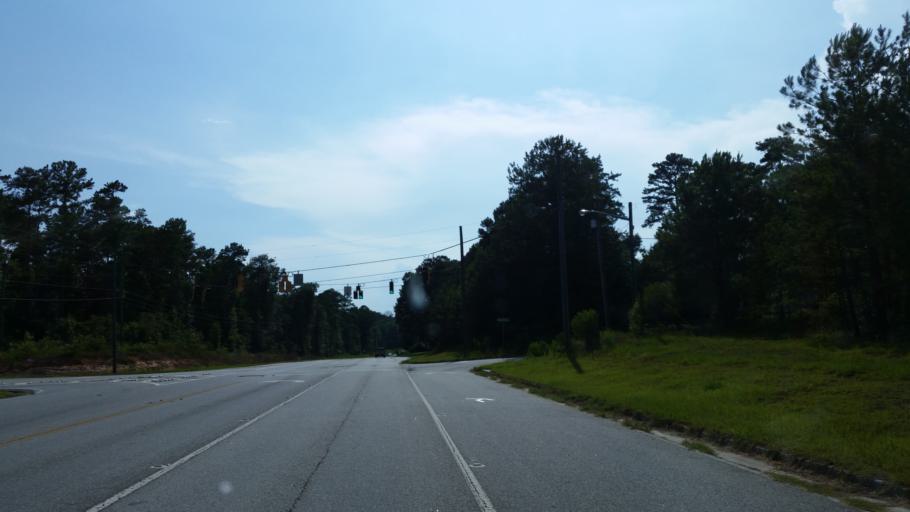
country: US
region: Georgia
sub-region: Lowndes County
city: Remerton
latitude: 30.8942
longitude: -83.3606
